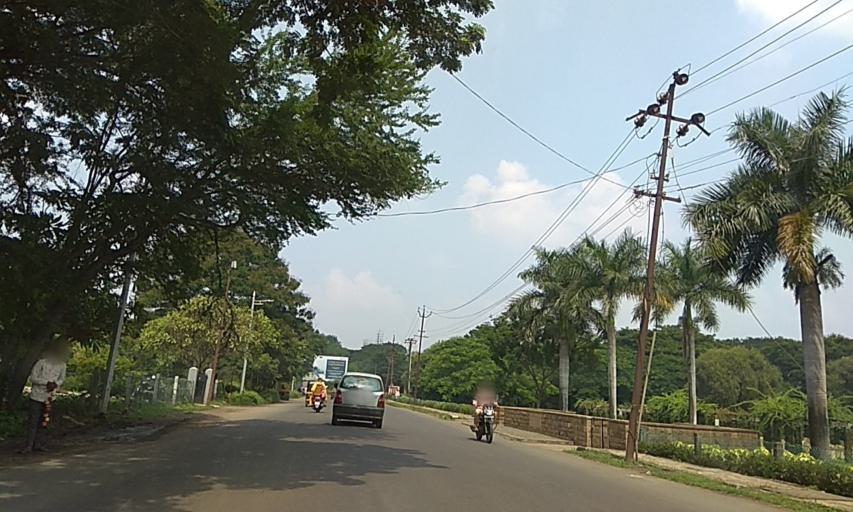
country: IN
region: Maharashtra
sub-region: Pune Division
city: Khadki
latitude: 18.5518
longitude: 73.8562
